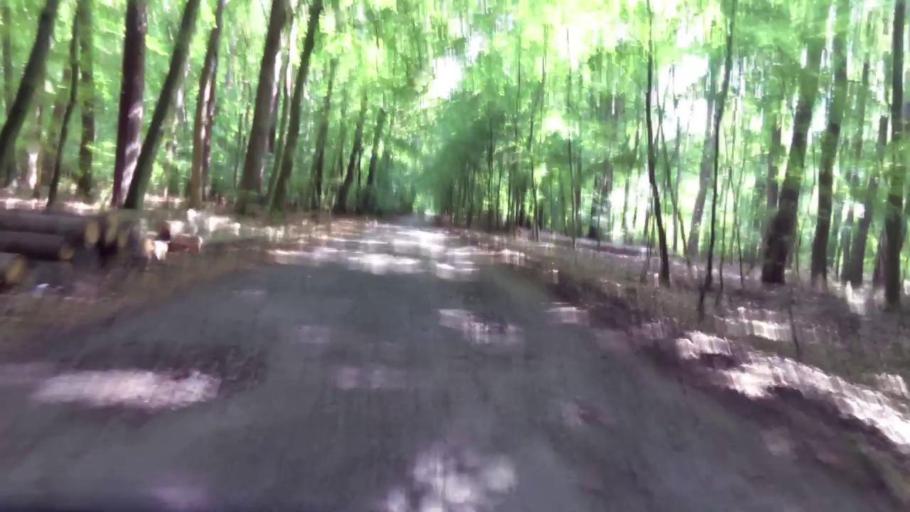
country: PL
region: West Pomeranian Voivodeship
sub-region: Powiat kamienski
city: Miedzyzdroje
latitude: 53.8817
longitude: 14.4809
